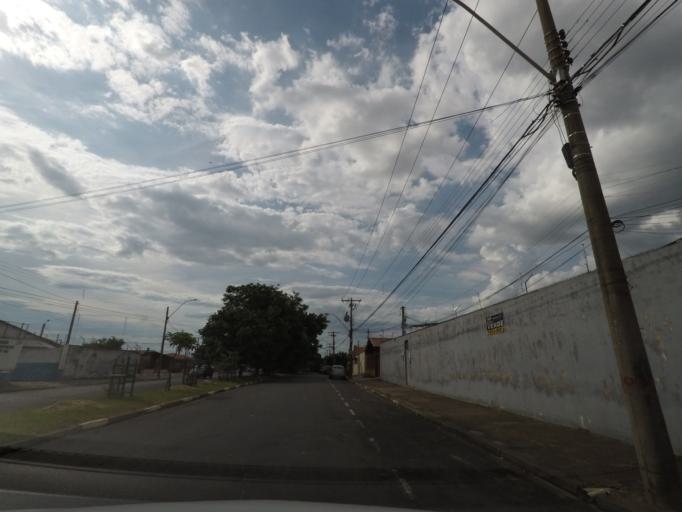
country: BR
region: Sao Paulo
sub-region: Campinas
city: Campinas
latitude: -22.8904
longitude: -47.1063
